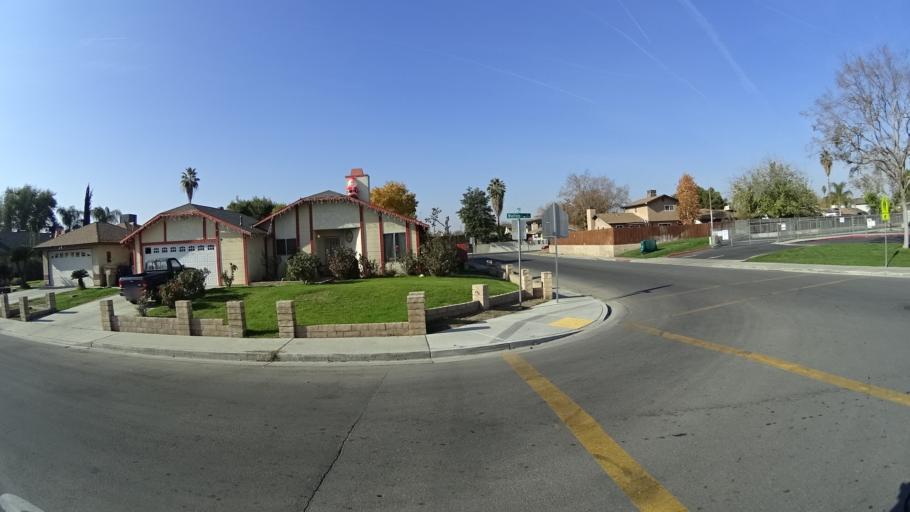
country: US
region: California
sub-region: Kern County
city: Greenfield
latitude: 35.3066
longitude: -119.0273
